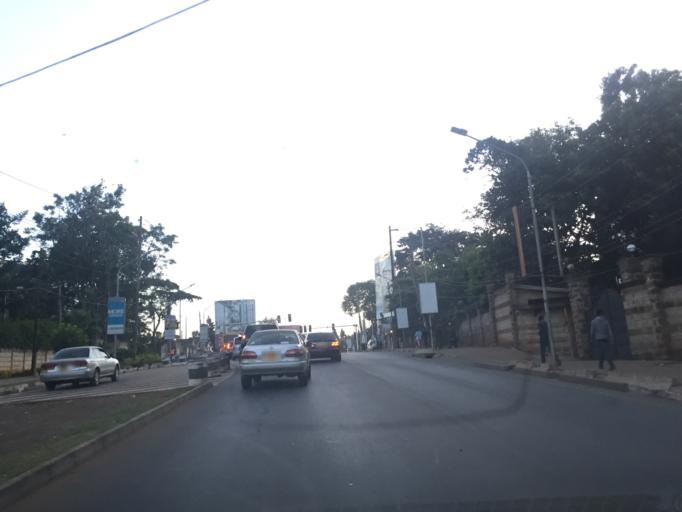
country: KE
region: Nairobi Area
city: Nairobi
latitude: -1.2706
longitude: 36.8017
